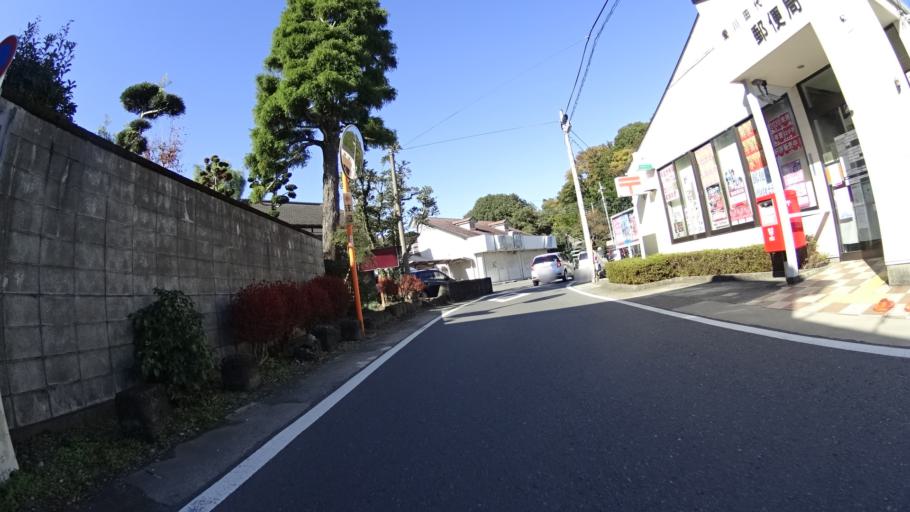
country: JP
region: Kanagawa
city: Zama
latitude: 35.5269
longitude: 139.2894
